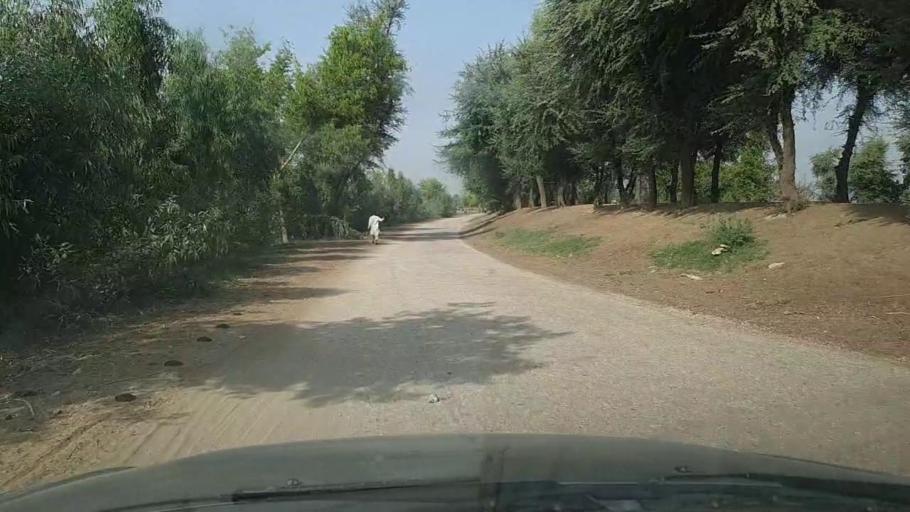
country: PK
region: Sindh
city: Pir jo Goth
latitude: 27.5164
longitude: 68.4766
